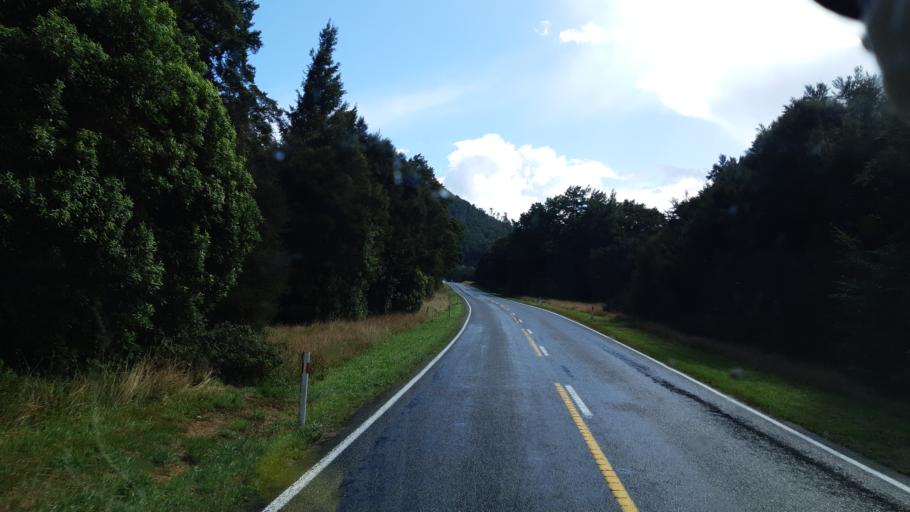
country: NZ
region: West Coast
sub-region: Buller District
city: Westport
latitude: -42.3533
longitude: 172.2328
